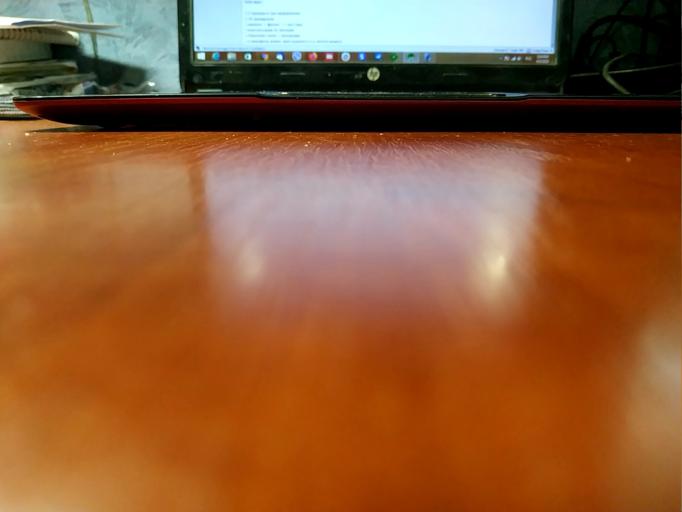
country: RU
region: Tverskaya
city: Sandovo
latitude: 58.5743
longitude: 36.4119
